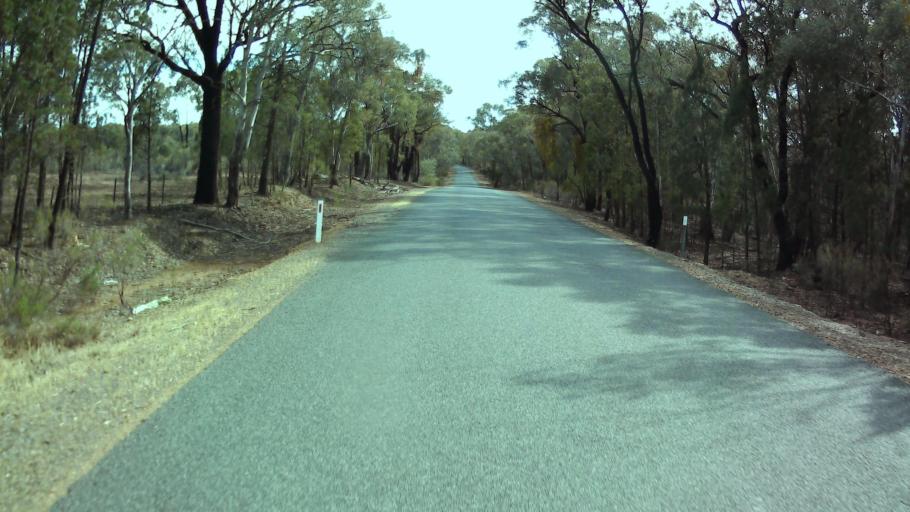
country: AU
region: New South Wales
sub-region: Weddin
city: Grenfell
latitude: -33.8863
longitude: 148.1970
